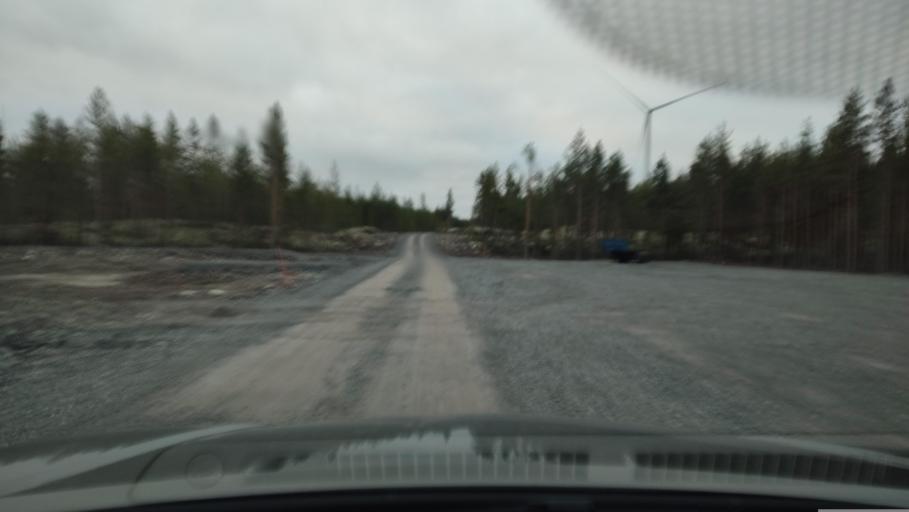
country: FI
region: Southern Ostrobothnia
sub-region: Suupohja
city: Karijoki
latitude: 62.1867
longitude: 21.5737
